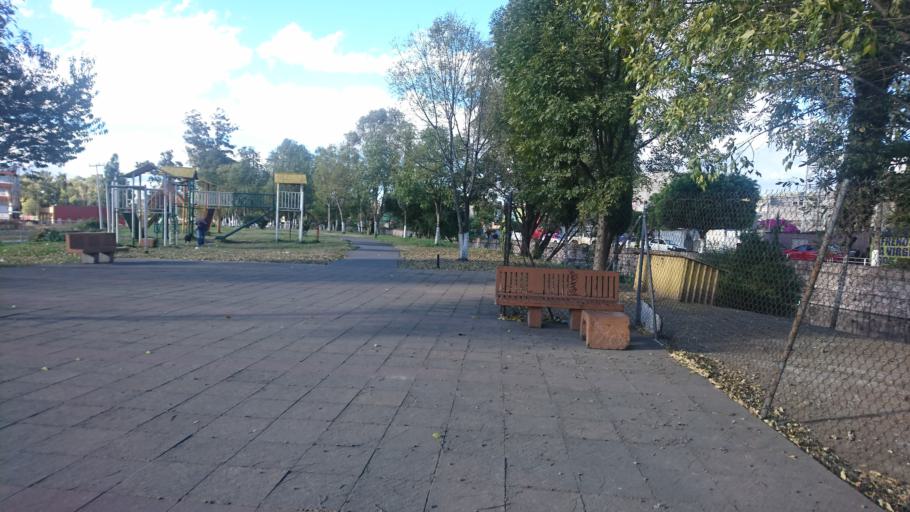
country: MX
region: Mexico City
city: Iztapalapa
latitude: 19.3208
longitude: -99.0994
